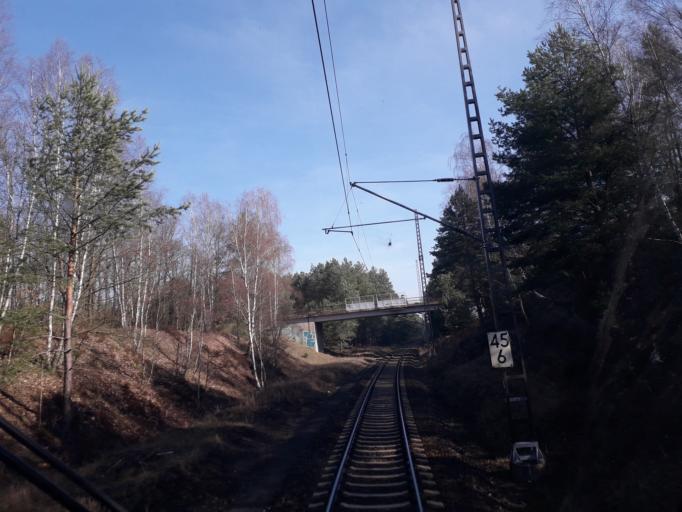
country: DE
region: Brandenburg
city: Beelitz
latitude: 52.2881
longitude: 12.9539
